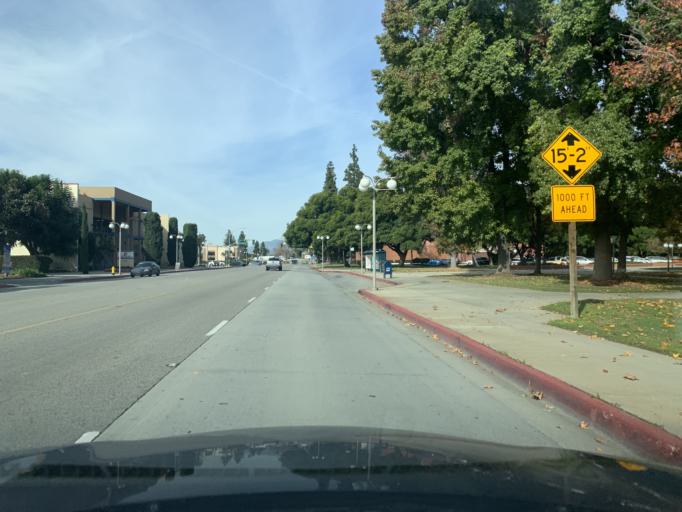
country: US
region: California
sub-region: Los Angeles County
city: West Covina
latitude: 34.0697
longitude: -117.9393
